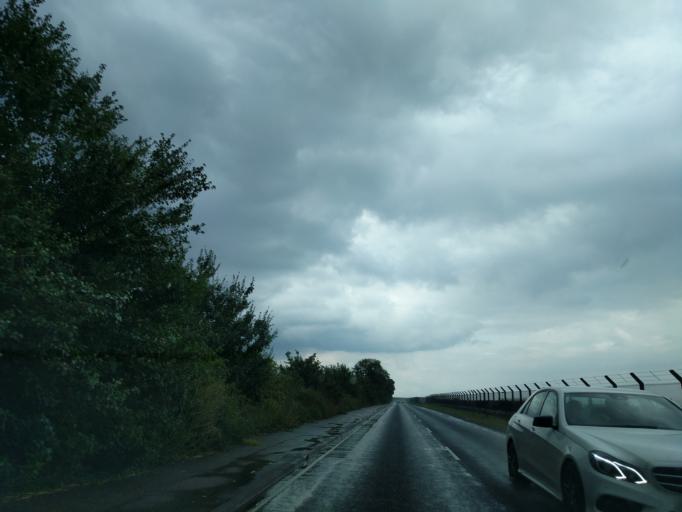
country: GB
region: England
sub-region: Suffolk
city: Lakenheath
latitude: 52.3648
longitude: 0.4921
